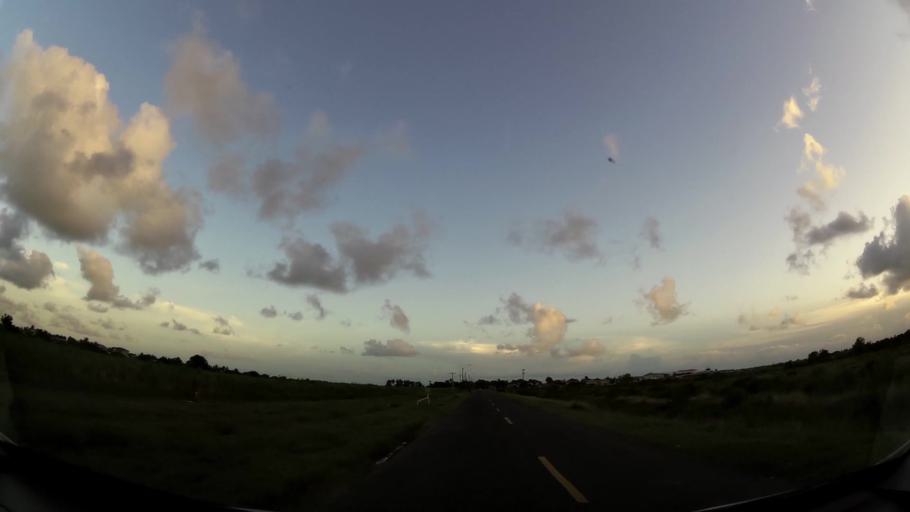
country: GY
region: Demerara-Mahaica
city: Georgetown
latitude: 6.8106
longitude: -58.1001
